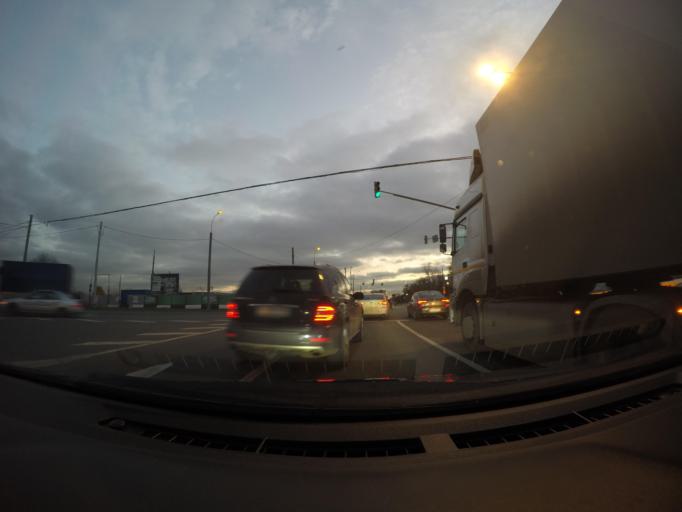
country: RU
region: Moscow
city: Kolomenskoye
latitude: 55.6680
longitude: 37.6608
